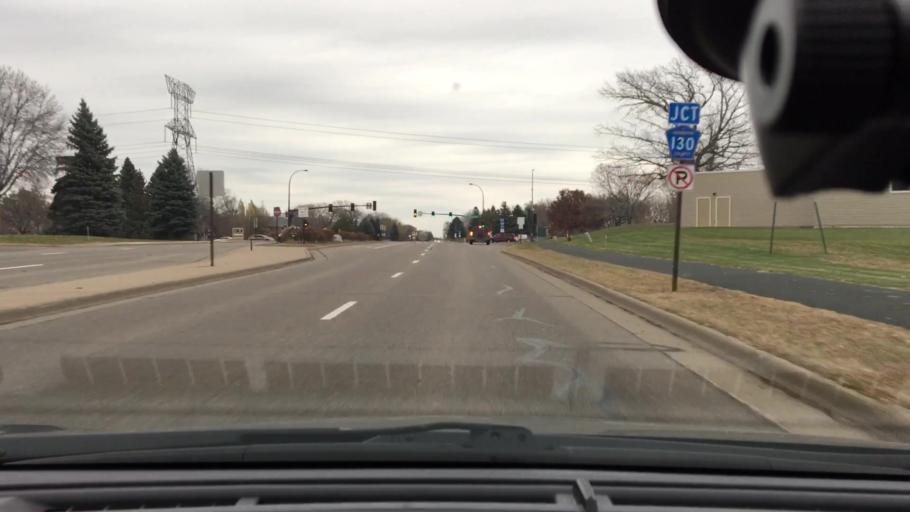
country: US
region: Minnesota
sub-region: Hennepin County
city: Osseo
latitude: 45.1234
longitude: -93.4499
